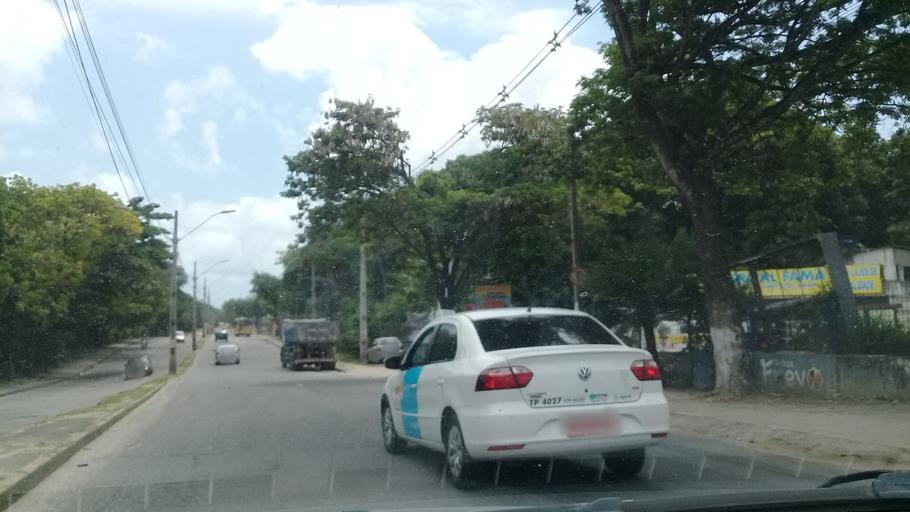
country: BR
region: Pernambuco
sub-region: Recife
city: Recife
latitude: -8.1086
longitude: -34.9340
